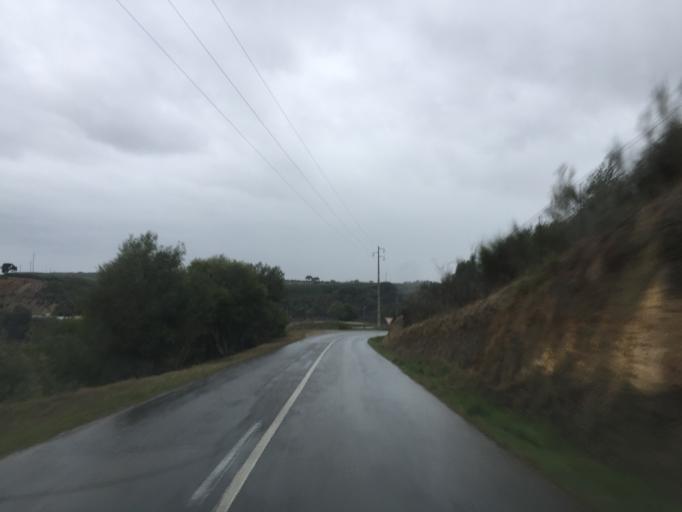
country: PT
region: Portalegre
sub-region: Avis
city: Avis
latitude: 39.0647
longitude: -7.8948
